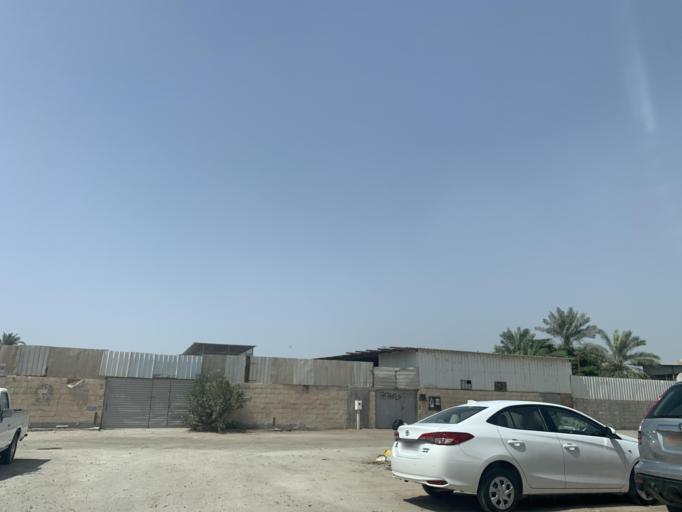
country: BH
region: Central Governorate
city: Madinat Hamad
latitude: 26.1502
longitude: 50.4959
